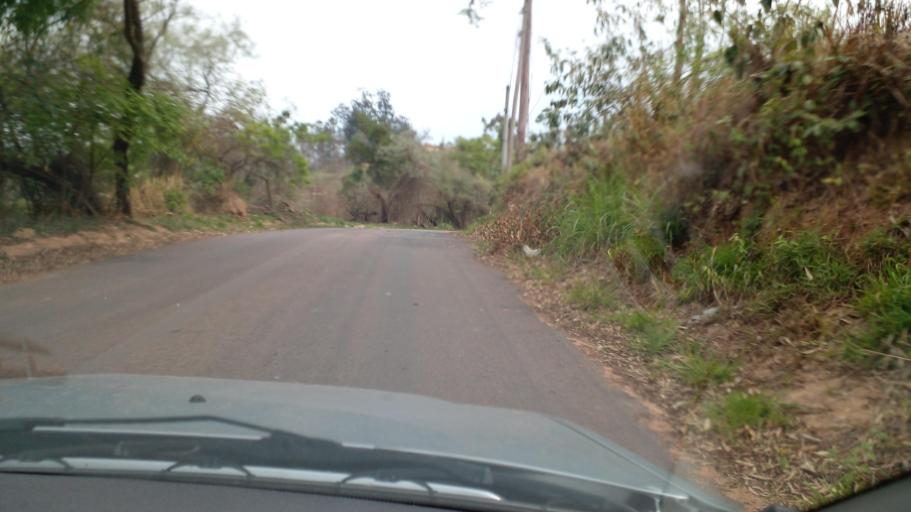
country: BR
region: Sao Paulo
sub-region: Louveira
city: Louveira
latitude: -23.1205
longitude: -46.8949
